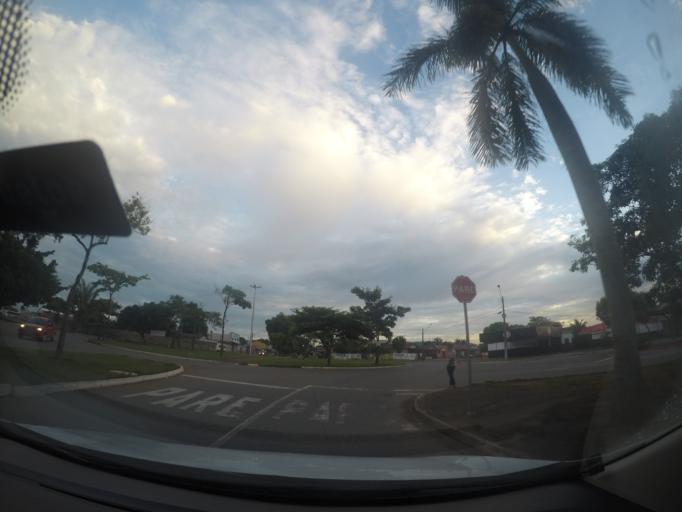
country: BR
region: Goias
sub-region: Goiania
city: Goiania
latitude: -16.6910
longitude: -49.3509
